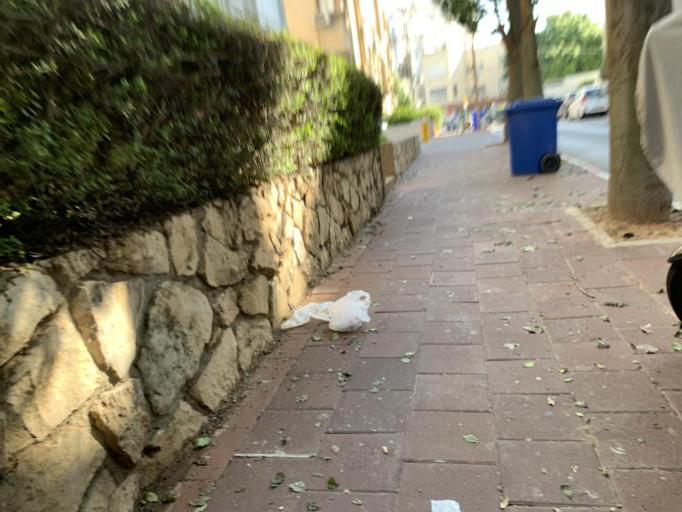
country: IL
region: Tel Aviv
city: Ramat Gan
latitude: 32.0887
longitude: 34.8053
